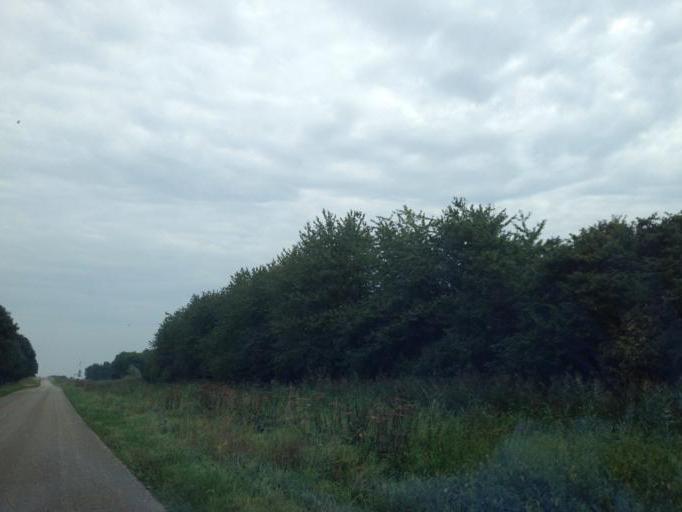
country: NL
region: Flevoland
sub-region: Gemeente Almere
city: Almere Stad
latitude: 52.3747
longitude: 5.2970
